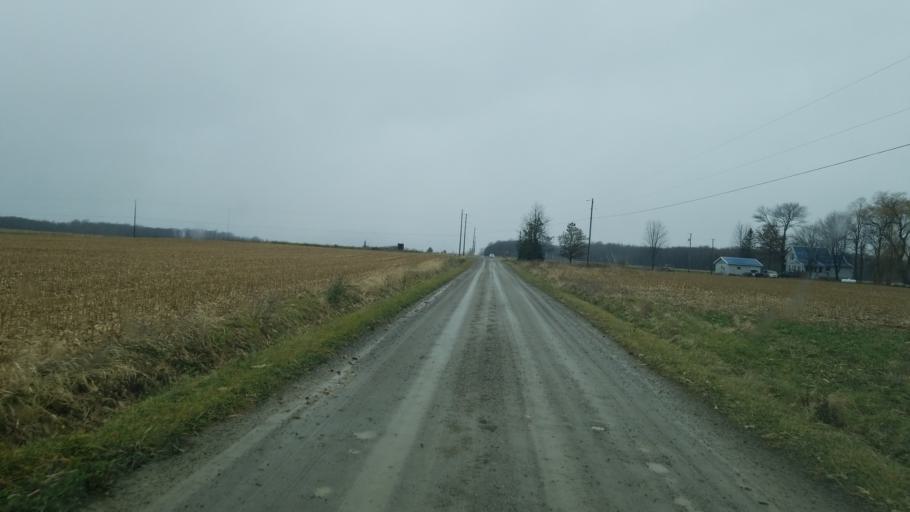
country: US
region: Ohio
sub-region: Ashtabula County
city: Roaming Shores
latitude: 41.5890
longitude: -80.7053
